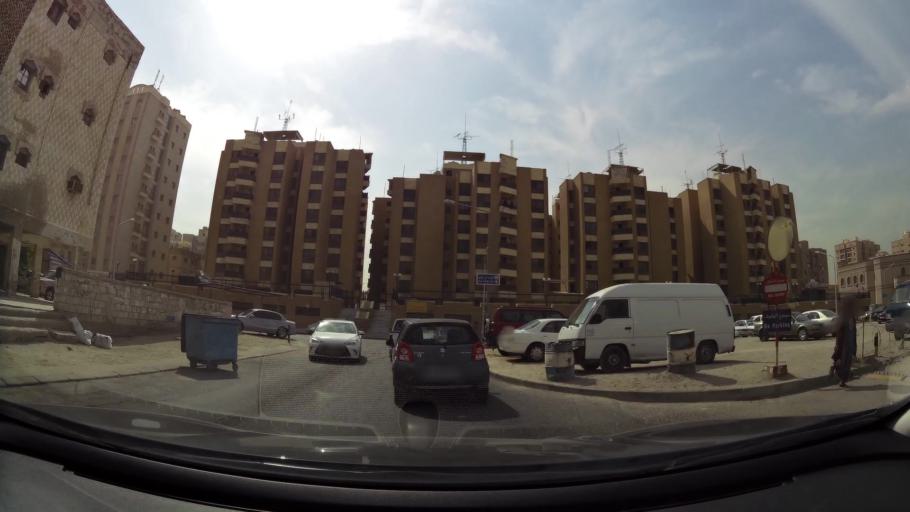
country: KW
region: Al Farwaniyah
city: Janub as Surrah
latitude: 29.2808
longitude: 47.9723
